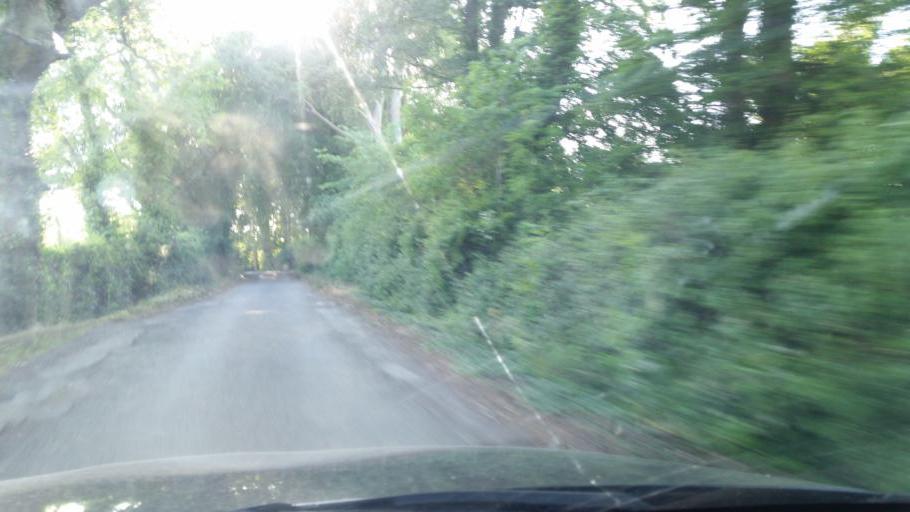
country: IE
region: Leinster
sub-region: Dublin City
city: Finglas
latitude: 53.4573
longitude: -6.3192
